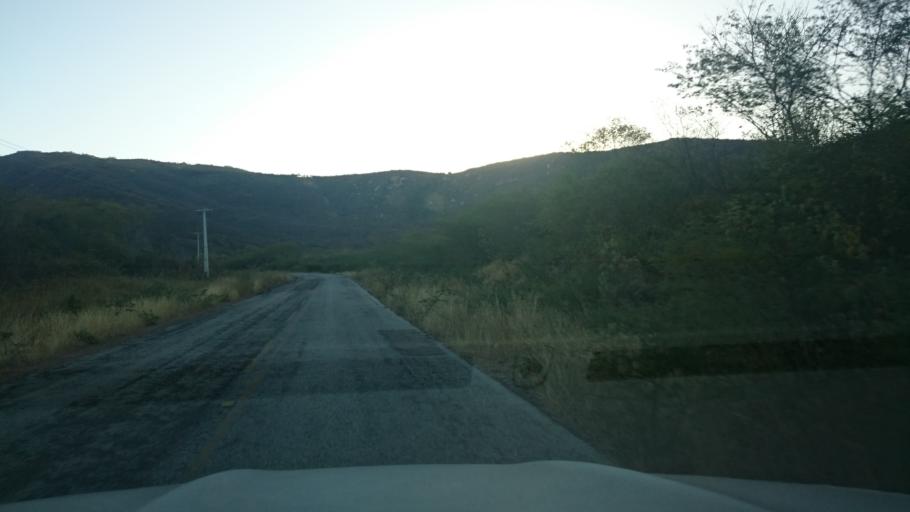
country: BR
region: Rio Grande do Norte
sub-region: Umarizal
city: Umarizal
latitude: -5.9918
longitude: -37.9636
